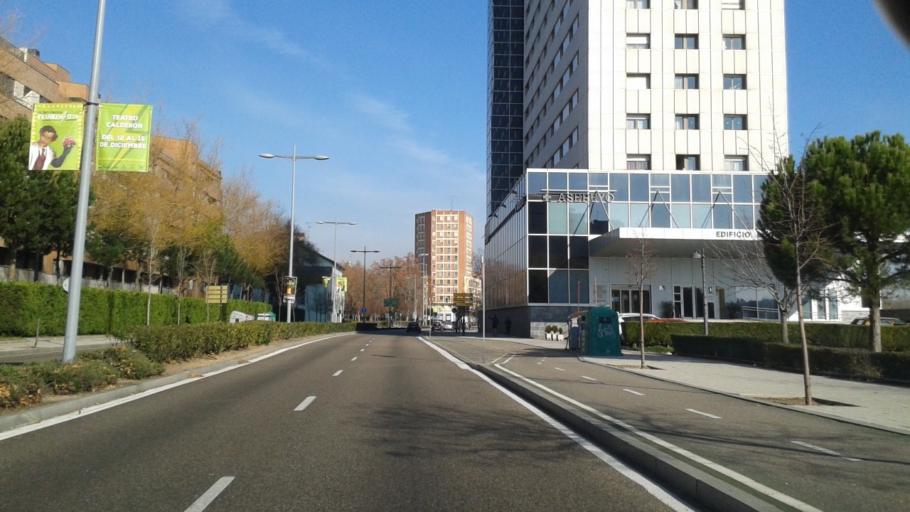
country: ES
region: Castille and Leon
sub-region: Provincia de Valladolid
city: Valladolid
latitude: 41.6584
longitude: -4.7350
